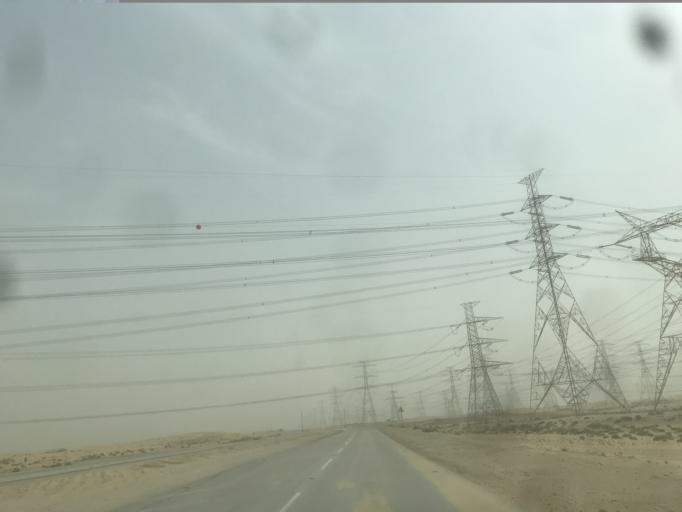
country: SA
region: Eastern Province
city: Abqaiq
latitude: 25.9064
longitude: 49.9086
